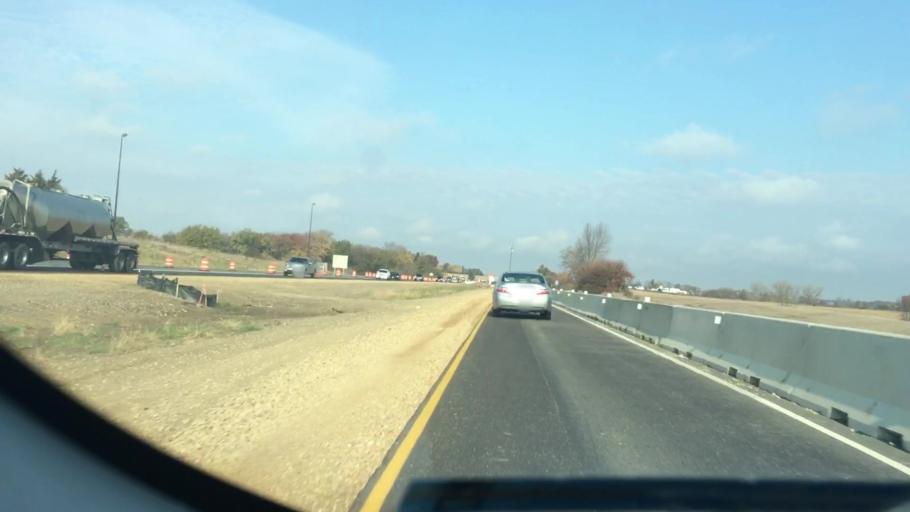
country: US
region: Illinois
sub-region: McLean County
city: Danvers
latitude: 40.5846
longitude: -89.1440
